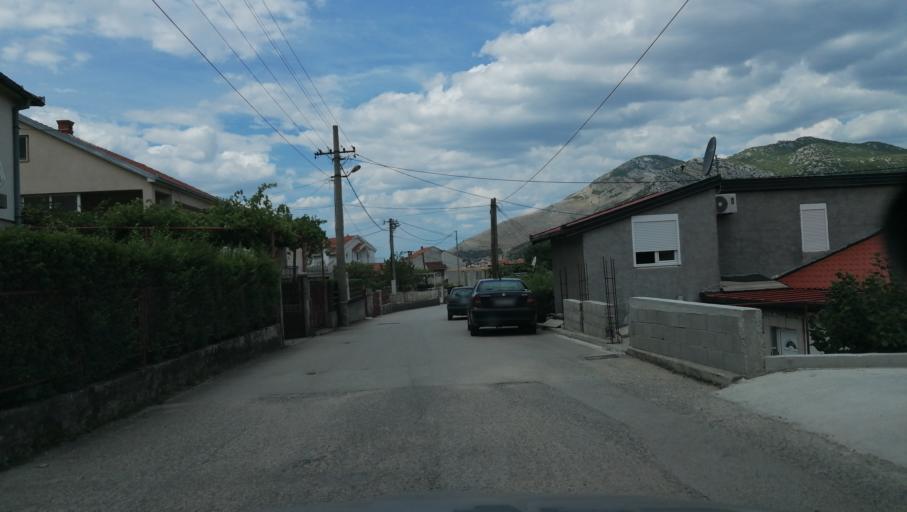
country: BA
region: Republika Srpska
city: Trebinje
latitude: 42.7120
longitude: 18.3560
